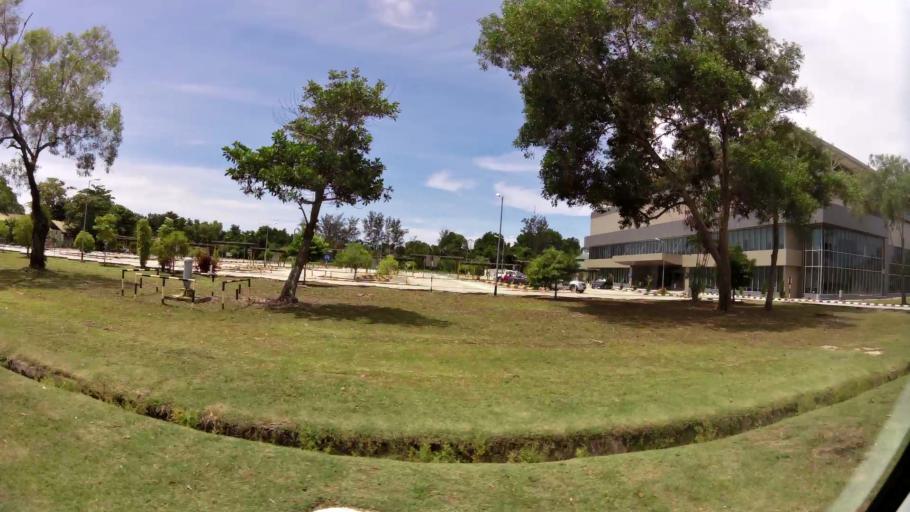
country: BN
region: Belait
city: Seria
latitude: 4.6078
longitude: 114.2944
